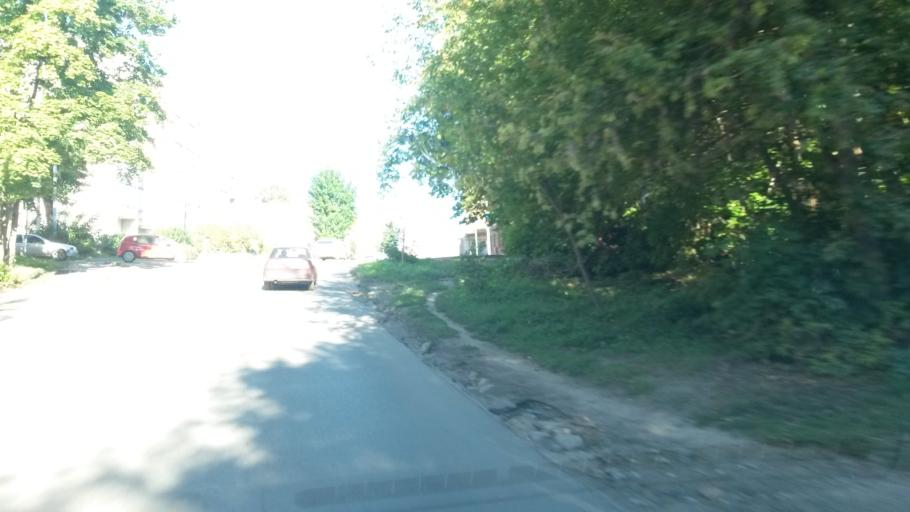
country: RU
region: Ivanovo
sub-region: Gorod Ivanovo
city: Ivanovo
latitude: 56.9905
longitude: 40.9782
